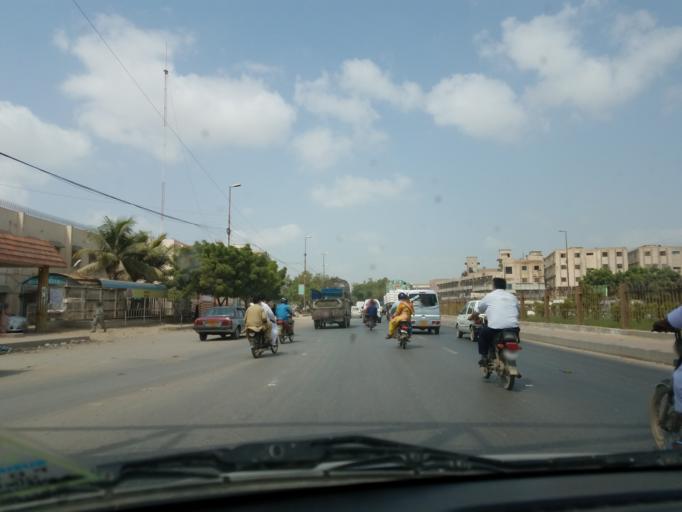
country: PK
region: Sindh
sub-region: Karachi District
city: Karachi
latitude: 24.9462
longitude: 67.0833
